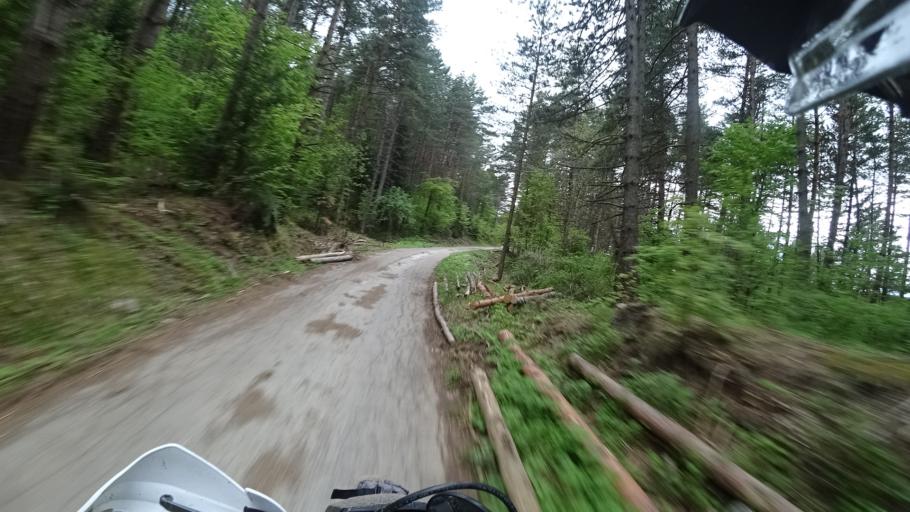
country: HR
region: Licko-Senjska
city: Jezerce
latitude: 44.8487
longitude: 15.4303
